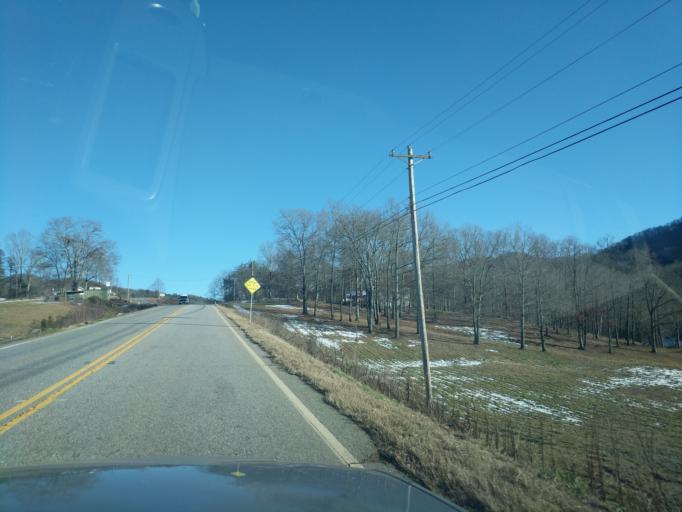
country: US
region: Georgia
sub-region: Towns County
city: Hiawassee
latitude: 34.9308
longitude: -83.6552
